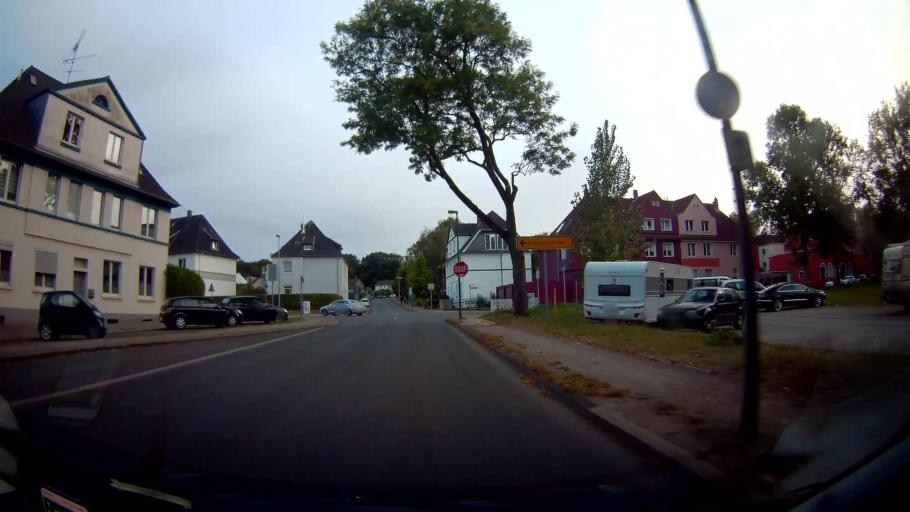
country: DE
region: North Rhine-Westphalia
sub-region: Regierungsbezirk Arnsberg
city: Herne
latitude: 51.5287
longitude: 7.2525
